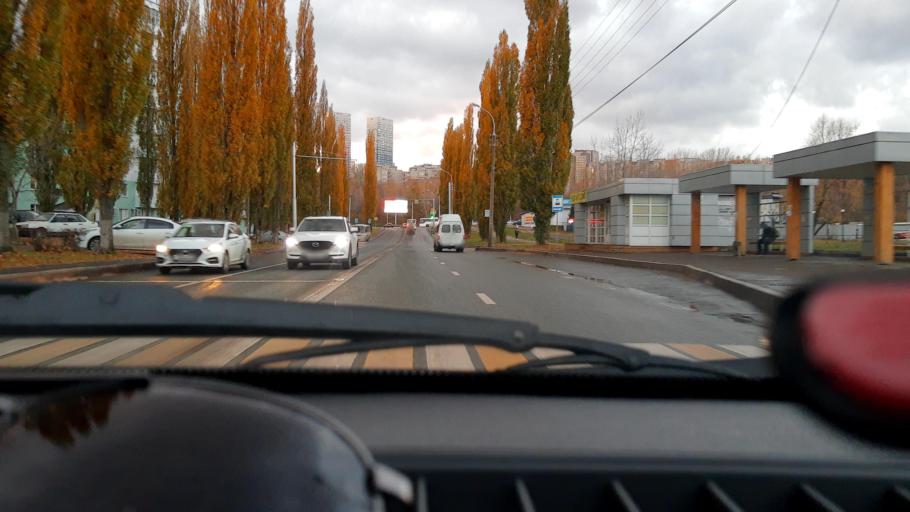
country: RU
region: Bashkortostan
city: Ufa
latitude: 54.7717
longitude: 56.0528
